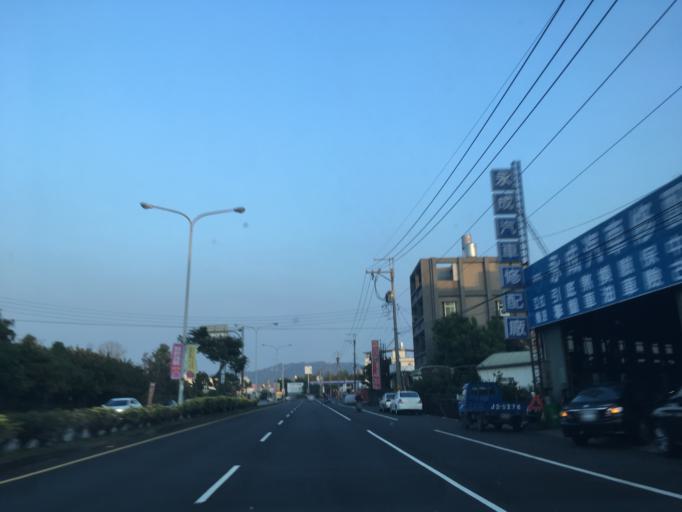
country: TW
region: Taiwan
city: Zhongxing New Village
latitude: 23.9900
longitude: 120.6692
